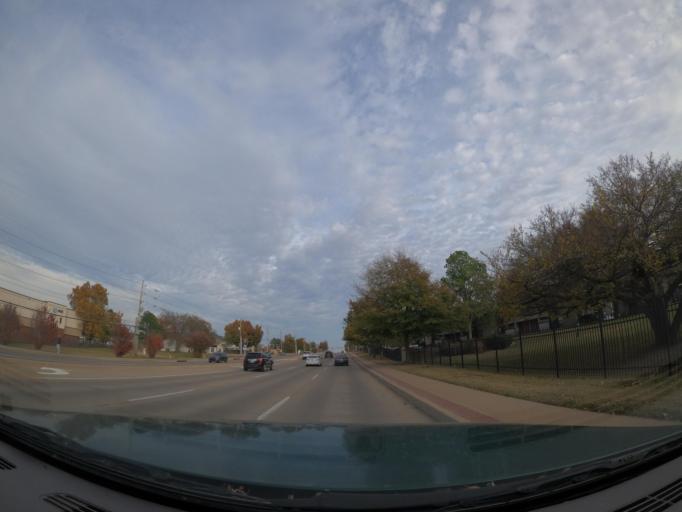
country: US
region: Oklahoma
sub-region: Tulsa County
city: Jenks
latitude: 36.0607
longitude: -95.9175
